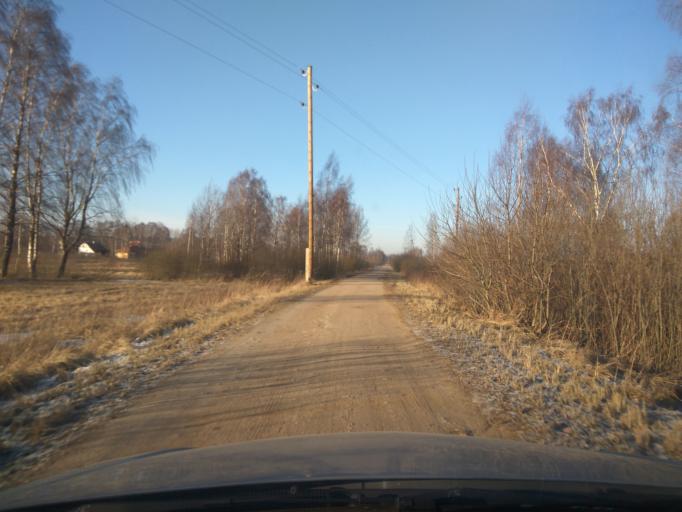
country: LV
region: Kuldigas Rajons
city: Kuldiga
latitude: 56.9592
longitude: 21.9664
